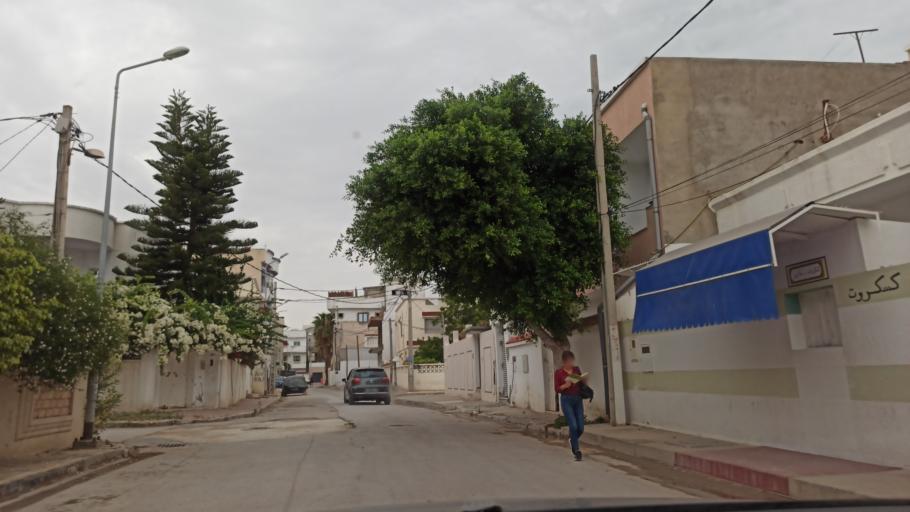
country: TN
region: Tunis
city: La Goulette
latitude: 36.8528
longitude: 10.2678
